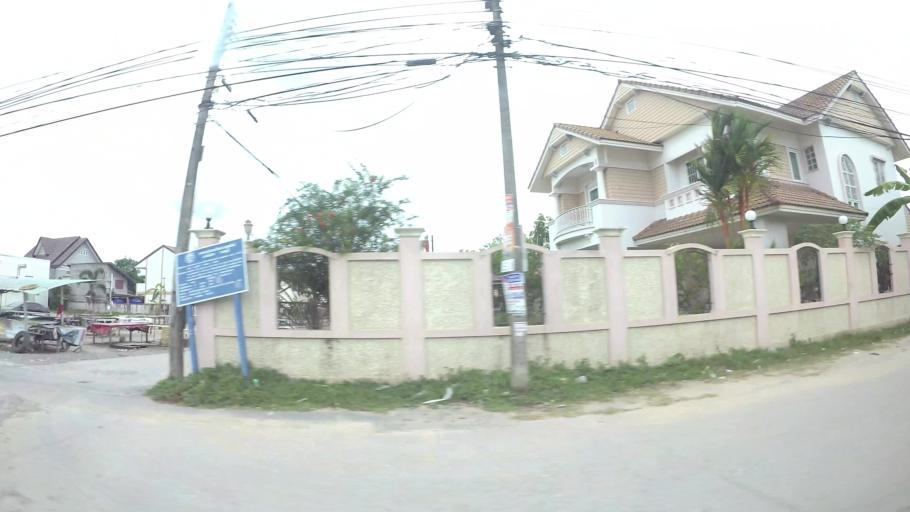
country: TH
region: Chon Buri
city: Si Racha
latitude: 13.1572
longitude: 100.9711
